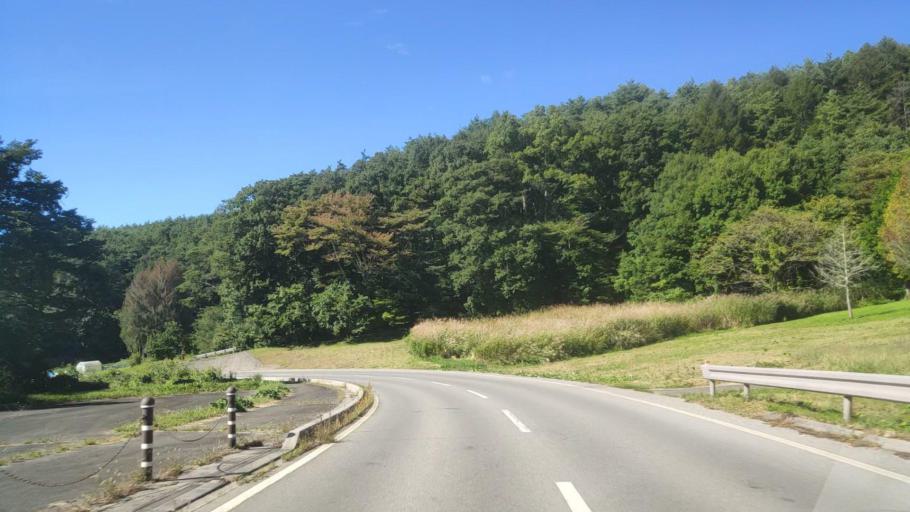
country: JP
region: Nagano
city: Chino
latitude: 35.9953
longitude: 138.2133
